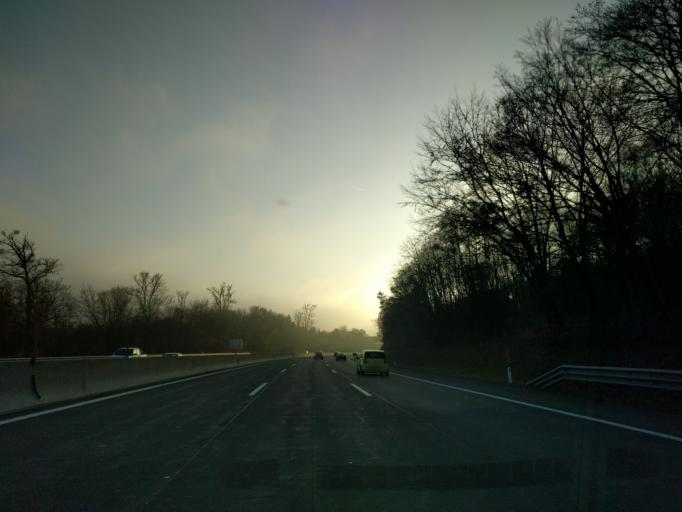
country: AT
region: Lower Austria
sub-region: Politischer Bezirk Wien-Umgebung
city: Purkersdorf
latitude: 48.1961
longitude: 16.2066
